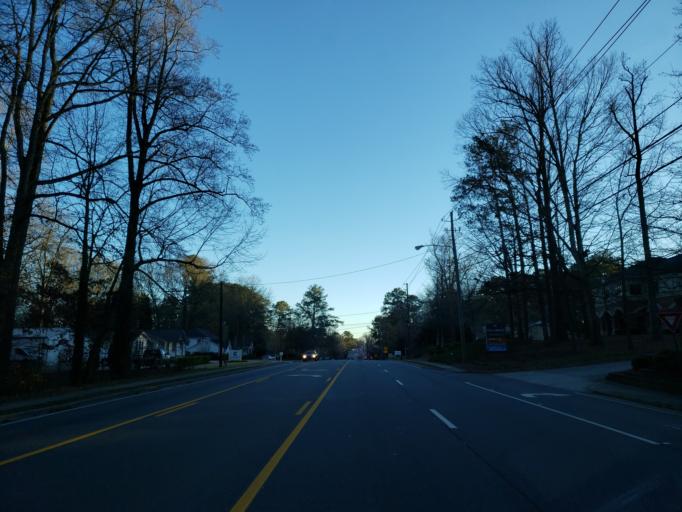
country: US
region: Georgia
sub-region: Fulton County
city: Alpharetta
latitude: 34.0856
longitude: -84.2951
